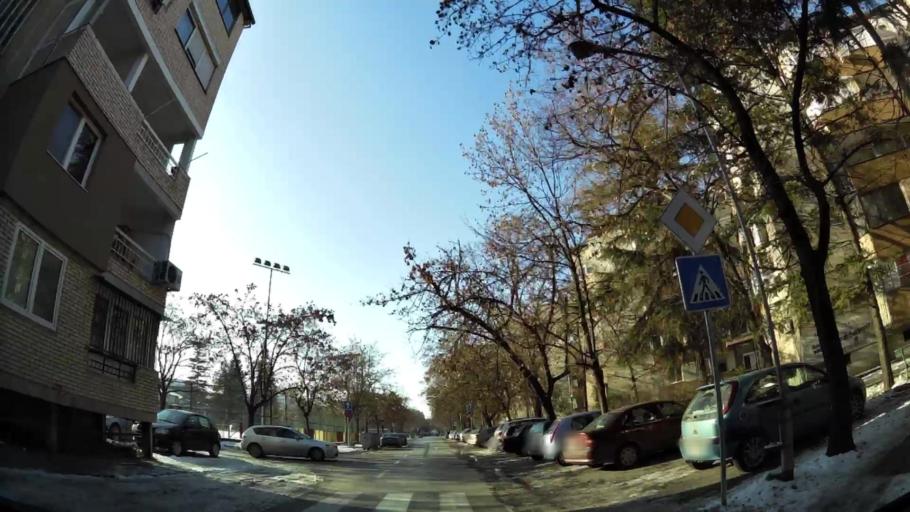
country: MK
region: Karpos
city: Skopje
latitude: 42.0072
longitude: 21.3893
